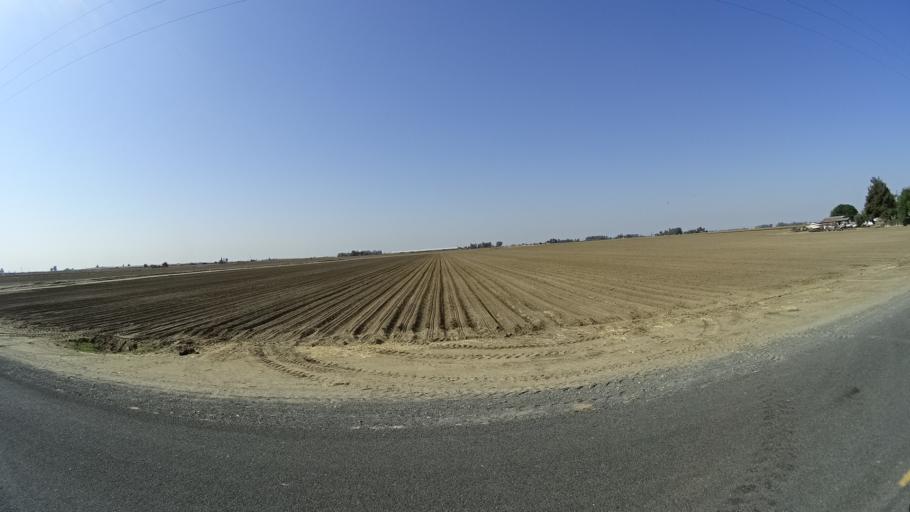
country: US
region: California
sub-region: Kings County
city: Home Garden
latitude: 36.2404
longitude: -119.6261
